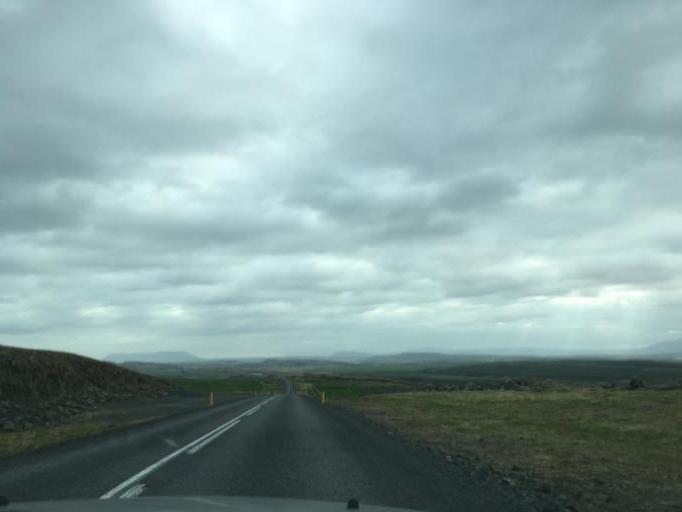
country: IS
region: South
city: Vestmannaeyjar
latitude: 64.2403
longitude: -20.2220
